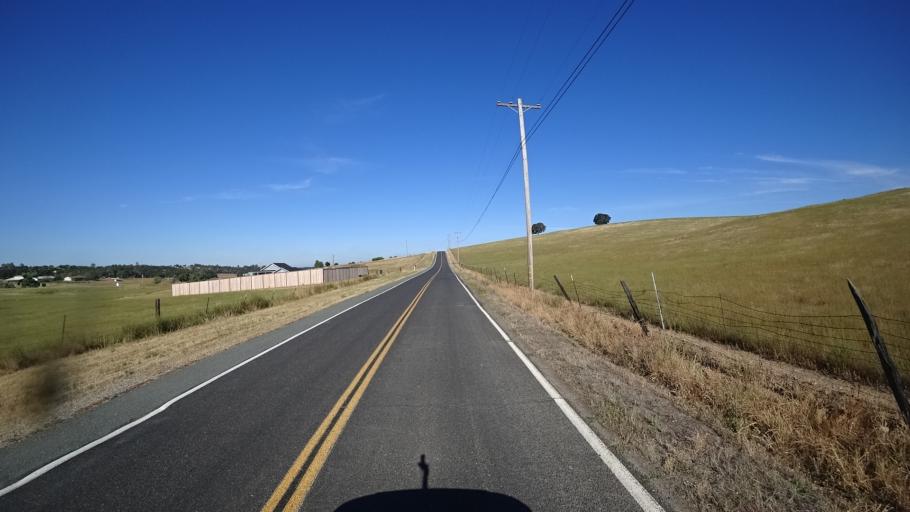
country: US
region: California
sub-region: Calaveras County
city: Valley Springs
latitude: 38.1893
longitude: -120.7992
